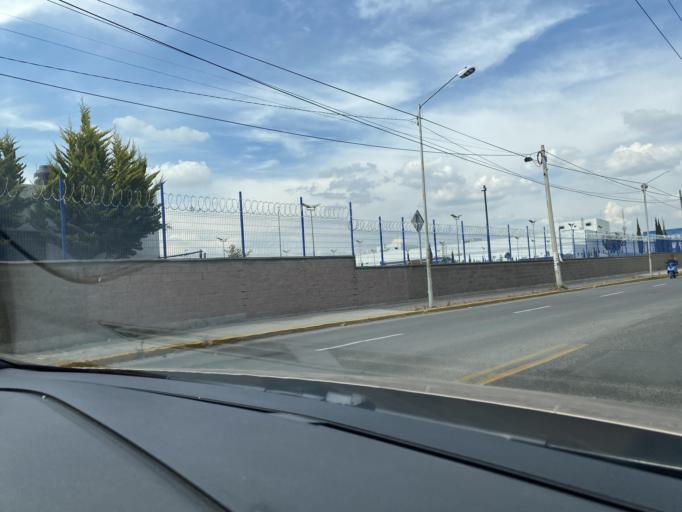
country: IN
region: Karnataka
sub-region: Dakshina Kannada
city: Puttur
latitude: 12.7366
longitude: 75.1855
